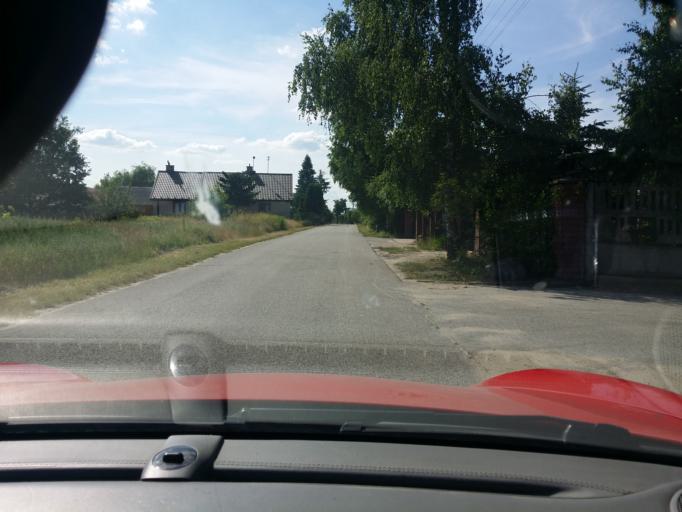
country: PL
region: Masovian Voivodeship
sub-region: Powiat radomski
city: Trablice
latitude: 51.3474
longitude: 21.1397
